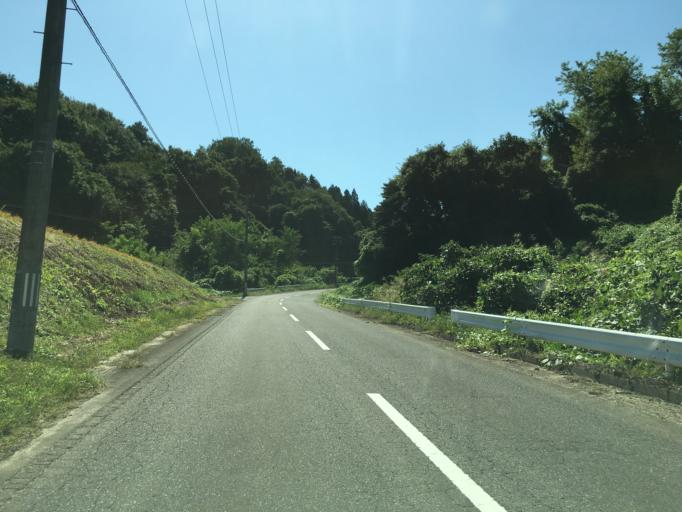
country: JP
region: Fukushima
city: Sukagawa
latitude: 37.2851
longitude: 140.4805
